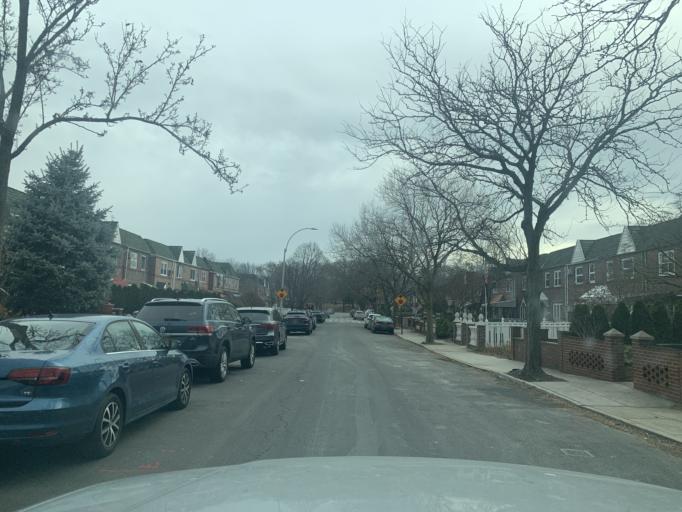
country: US
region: New York
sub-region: Kings County
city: East New York
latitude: 40.7231
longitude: -73.8799
